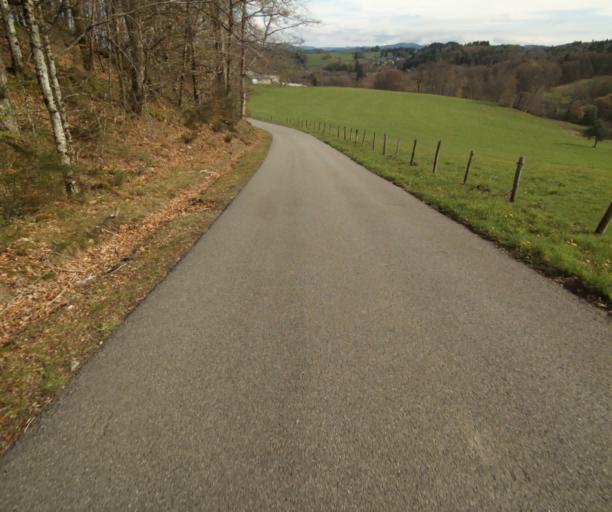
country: FR
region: Limousin
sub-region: Departement de la Correze
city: Correze
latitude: 45.3376
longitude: 1.8558
